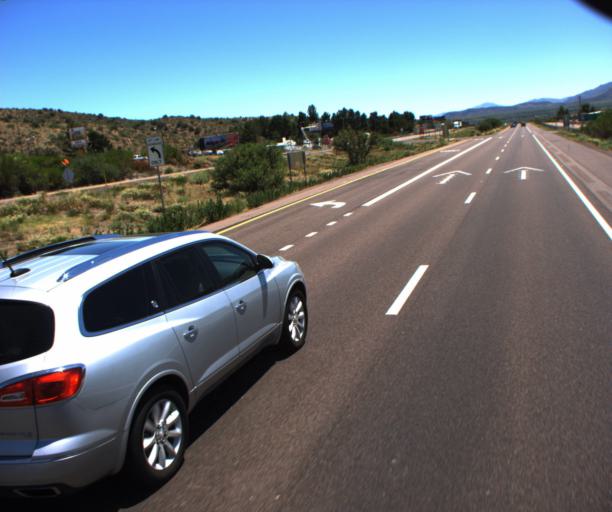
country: US
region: Arizona
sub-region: Gila County
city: Payson
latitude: 34.1087
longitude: -111.3539
